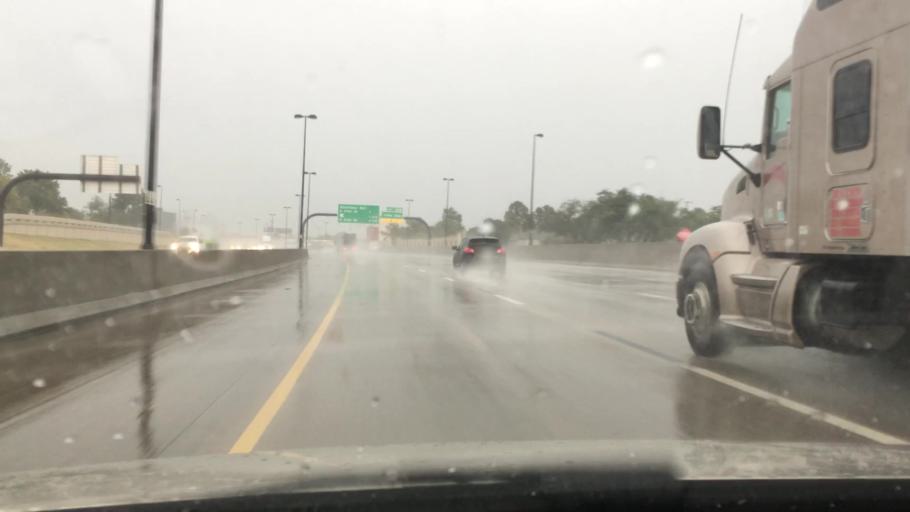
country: US
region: Oklahoma
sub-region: Tulsa County
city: Jenks
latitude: 36.0914
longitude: -95.9302
